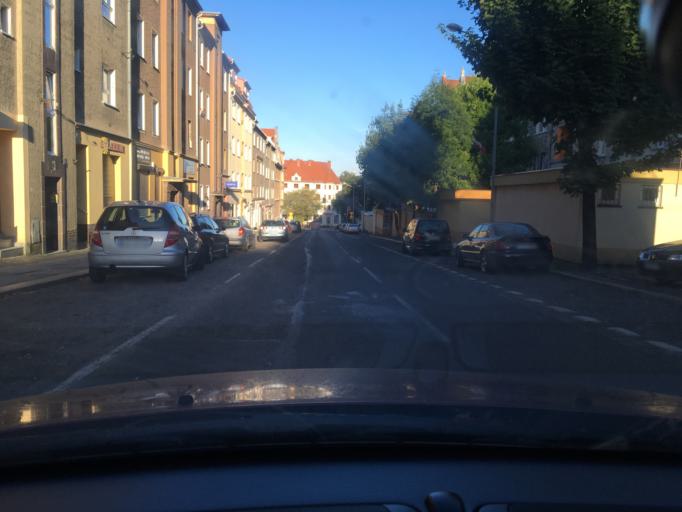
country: PL
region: Lower Silesian Voivodeship
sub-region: Powiat zgorzelecki
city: Zgorzelec
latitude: 51.1496
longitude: 15.0088
